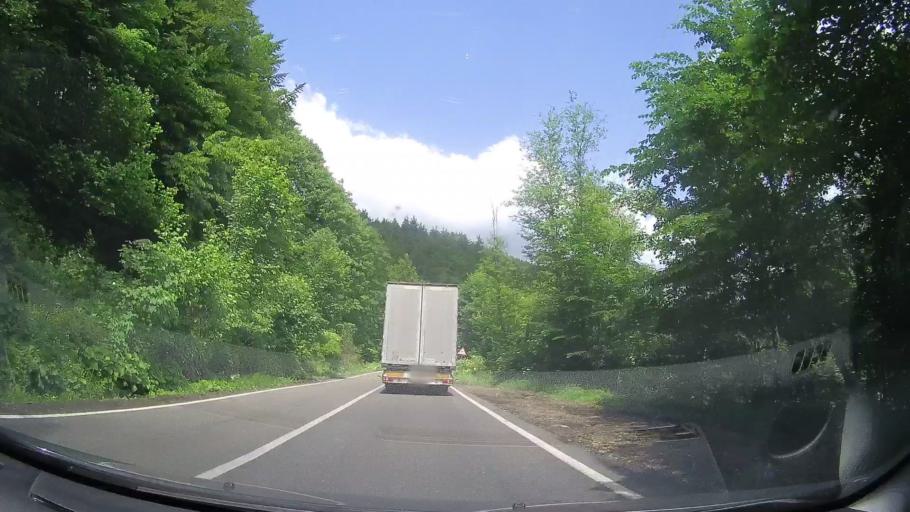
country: RO
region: Prahova
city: Maneciu
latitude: 45.3636
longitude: 25.9318
